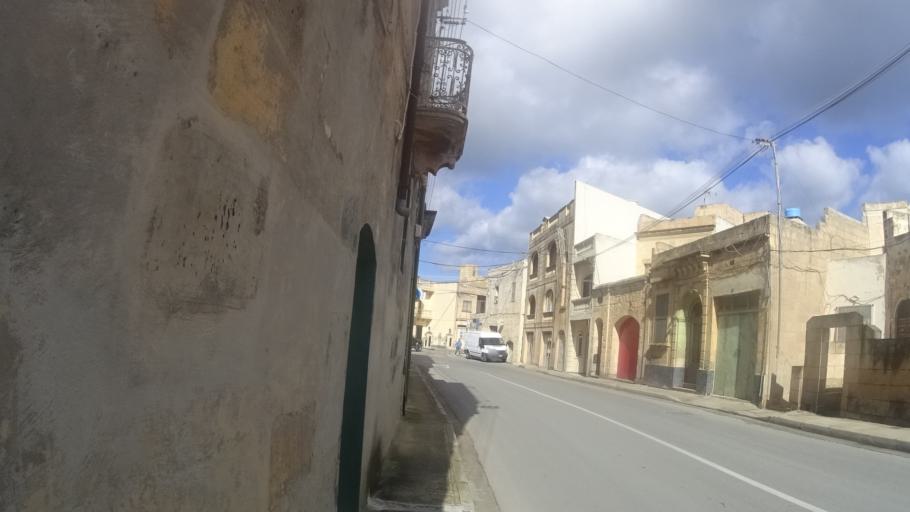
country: MT
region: In-Nadur
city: Nadur
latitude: 36.0394
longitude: 14.2886
